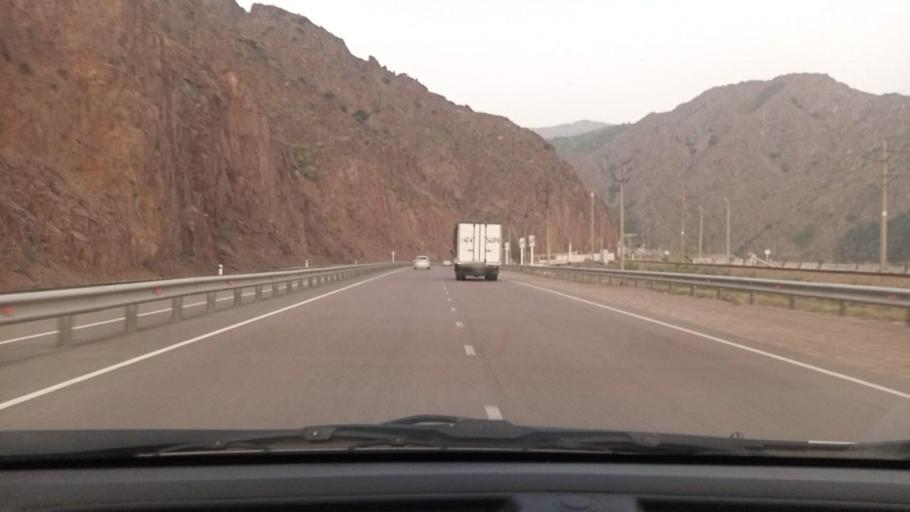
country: UZ
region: Toshkent
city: Angren
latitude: 41.0765
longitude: 70.3028
